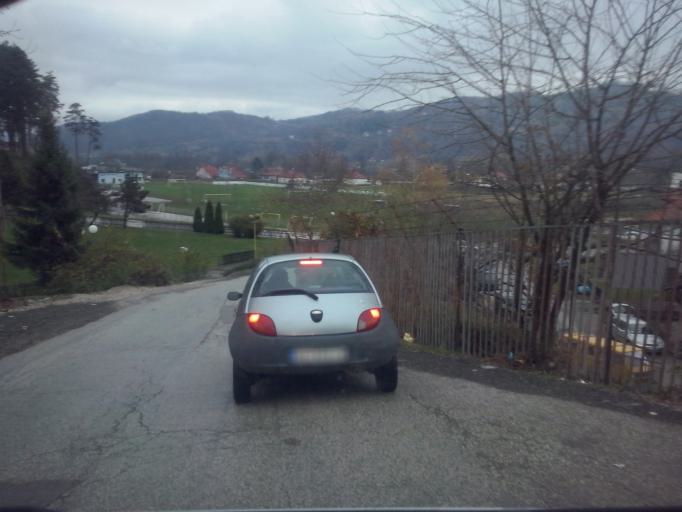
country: RS
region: Central Serbia
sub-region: Zlatiborski Okrug
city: Arilje
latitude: 43.7509
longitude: 20.1009
